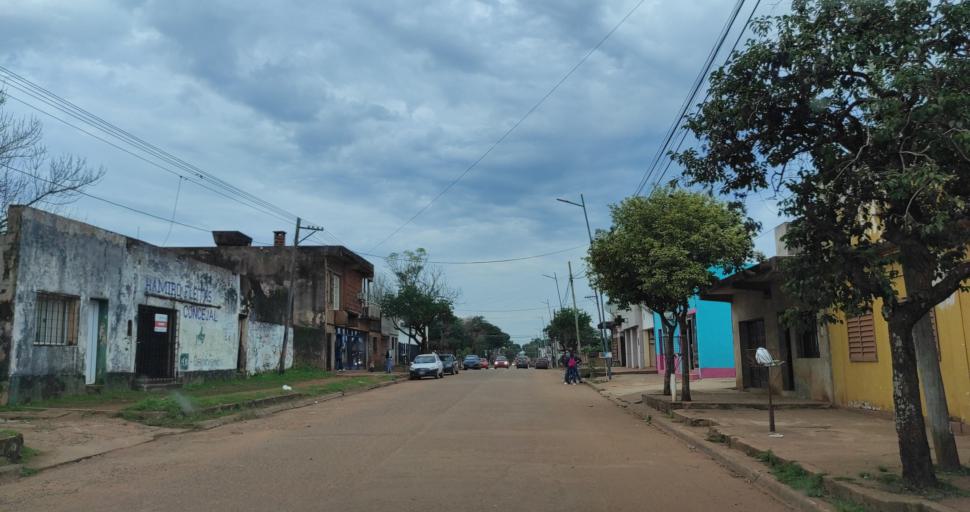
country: AR
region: Corrientes
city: Santo Tome
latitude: -28.5514
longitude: -56.0479
